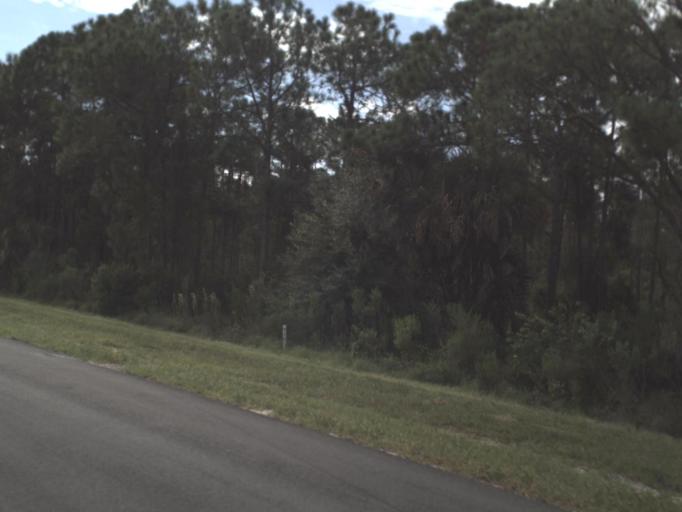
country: US
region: Florida
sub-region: Sarasota County
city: Warm Mineral Springs
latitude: 27.1003
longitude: -82.2837
